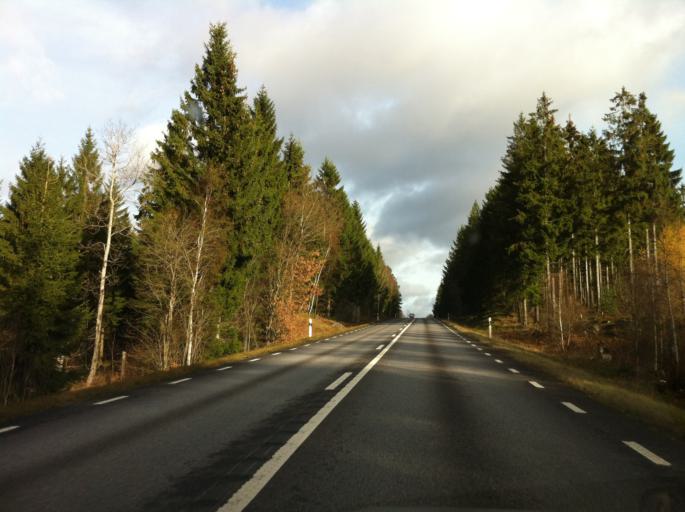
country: SE
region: Kronoberg
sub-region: Alvesta Kommun
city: Vislanda
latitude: 56.7381
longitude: 14.5051
